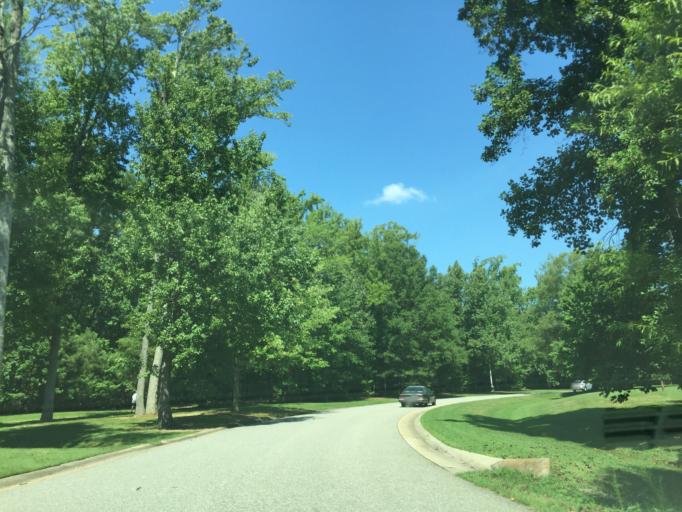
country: US
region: Virginia
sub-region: City of Newport News
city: Newport News
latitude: 37.0533
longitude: -76.4898
